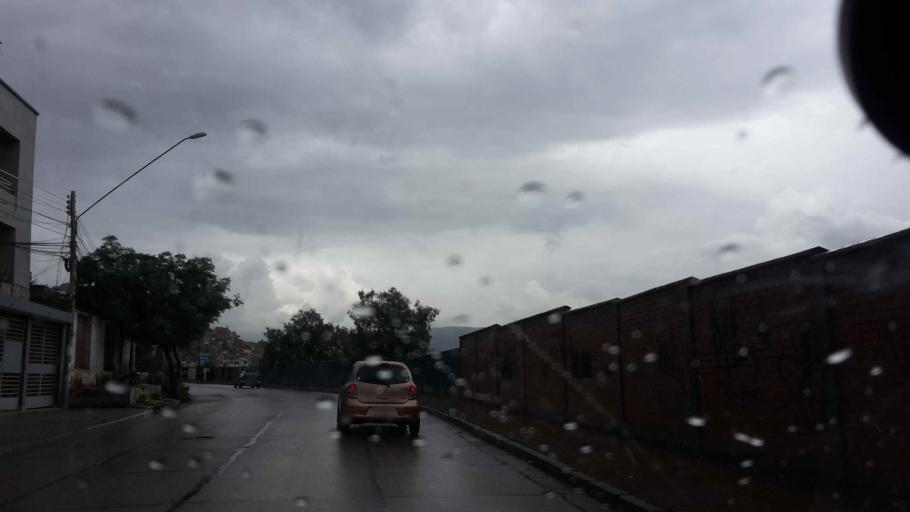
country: BO
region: Cochabamba
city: Cochabamba
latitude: -17.4152
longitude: -66.1502
